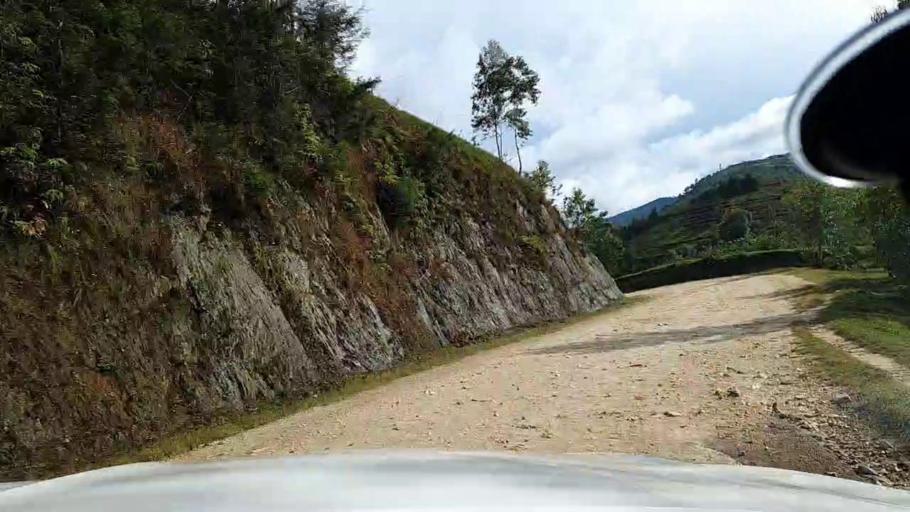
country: RW
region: Western Province
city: Kibuye
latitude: -2.1253
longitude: 29.4977
